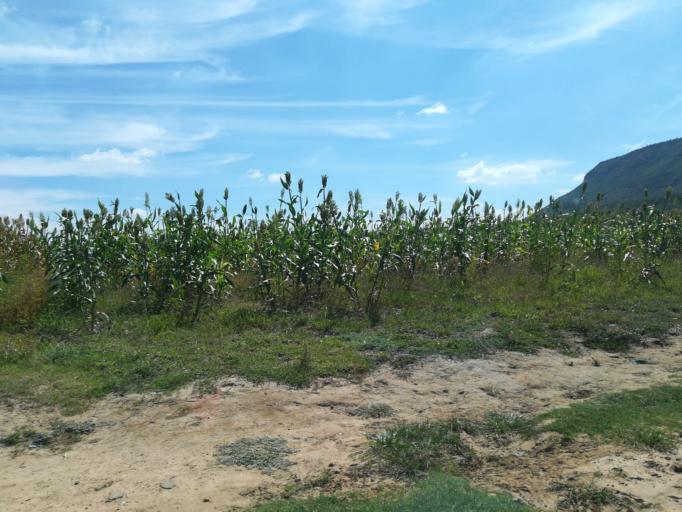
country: LS
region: Mohale's Hoek District
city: Mohale's Hoek
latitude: -30.1031
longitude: 27.4639
